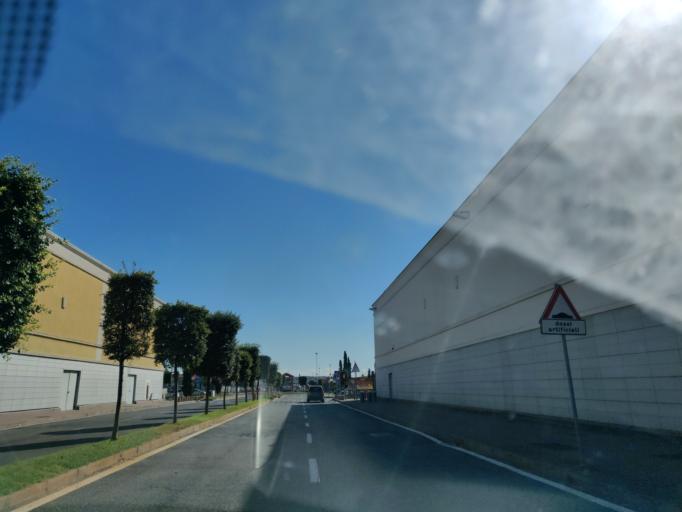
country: IT
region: Latium
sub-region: Citta metropolitana di Roma Capitale
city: Npp 23 (Parco Leonardo)
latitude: 41.8076
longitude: 12.2988
